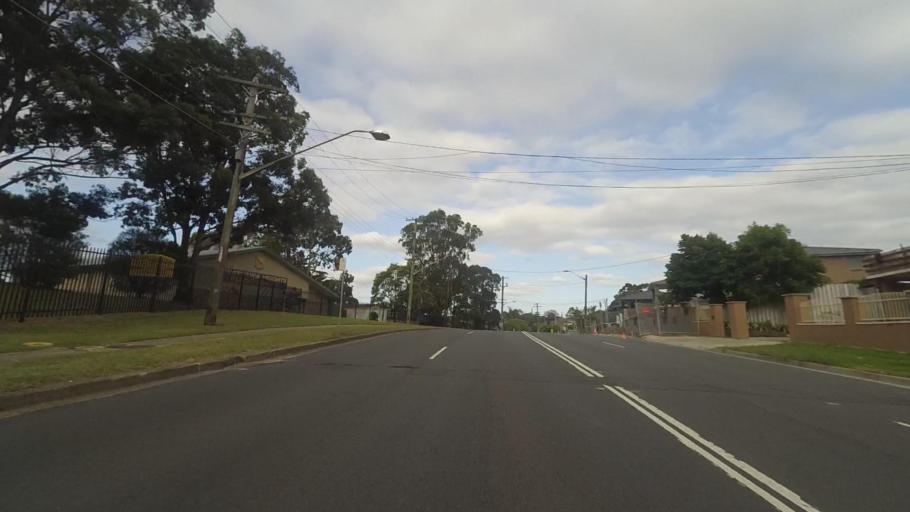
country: AU
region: New South Wales
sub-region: Bankstown
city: Bankstown
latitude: -33.9159
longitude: 151.0116
